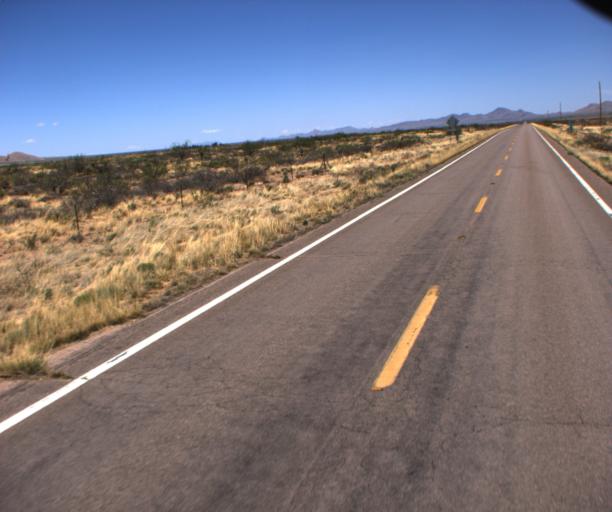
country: US
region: Arizona
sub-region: Cochise County
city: Douglas
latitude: 31.7681
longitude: -109.0789
